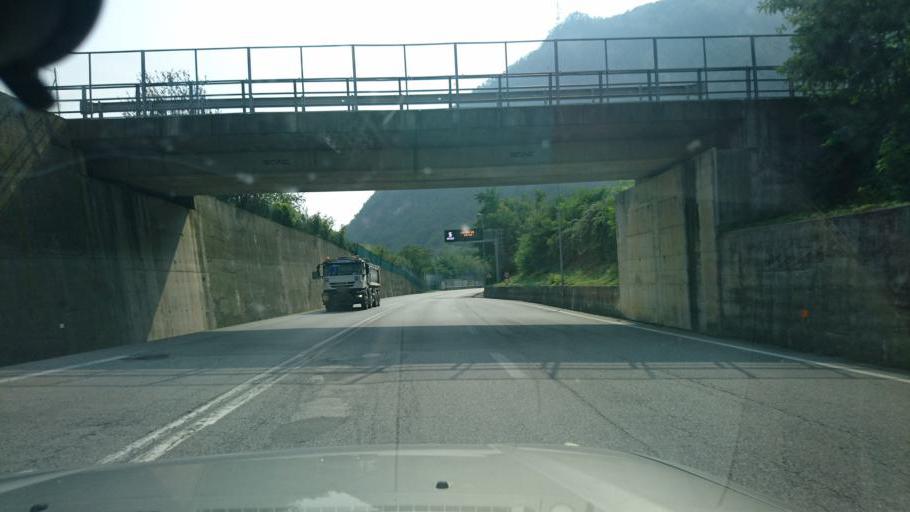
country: IT
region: Lombardy
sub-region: Provincia di Brescia
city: Roe
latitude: 45.6331
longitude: 10.4960
